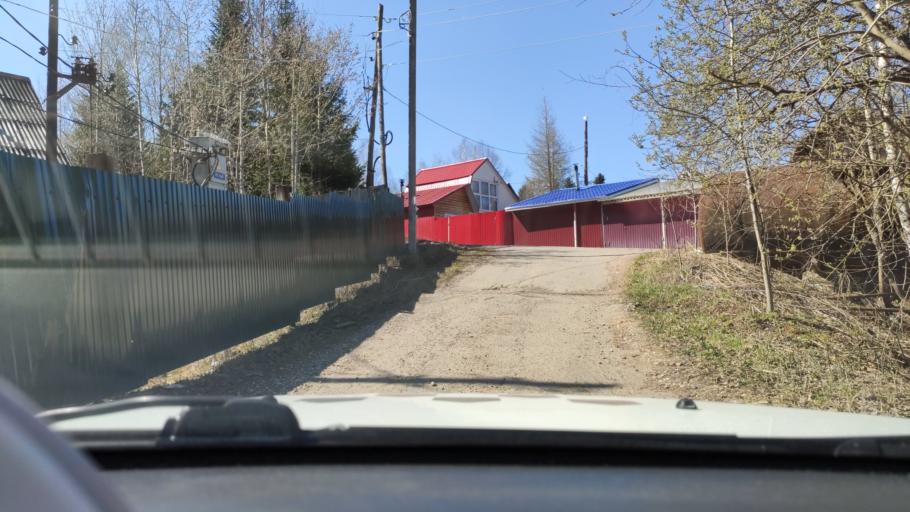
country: RU
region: Perm
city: Novyye Lyady
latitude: 58.0500
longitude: 56.6481
